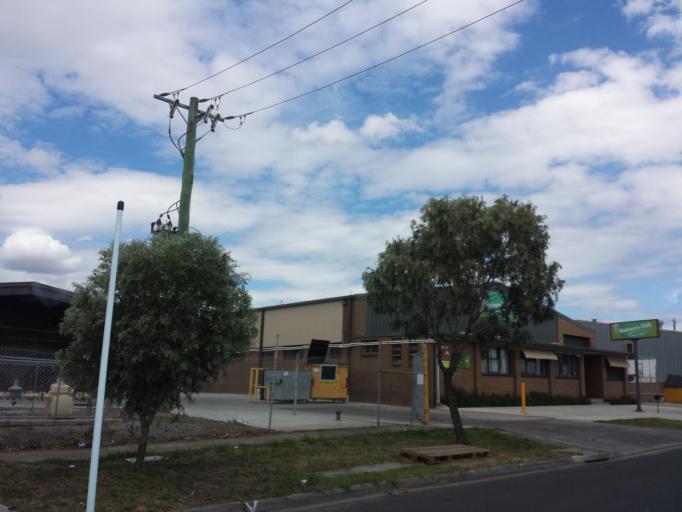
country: AU
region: Victoria
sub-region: Darebin
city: Reservoir
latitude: -37.6916
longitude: 144.9905
